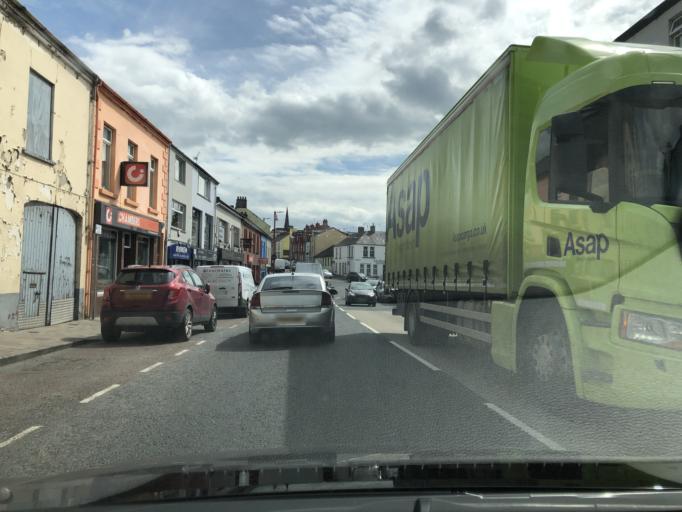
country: GB
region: Northern Ireland
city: Ballynahinch
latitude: 54.4015
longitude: -5.8973
